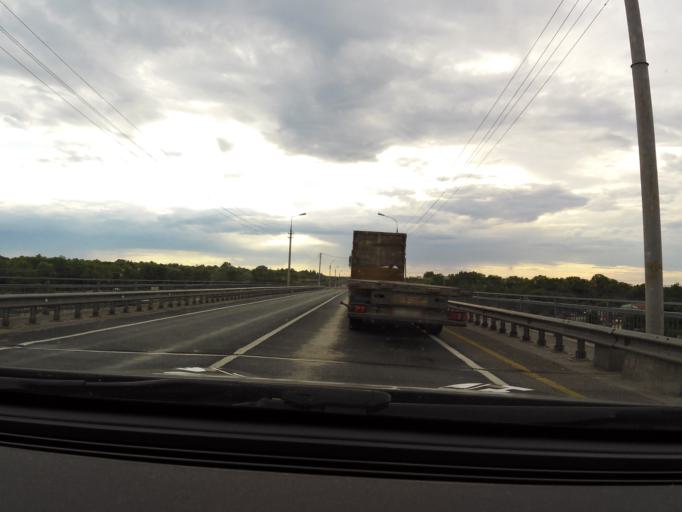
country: RU
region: Vladimir
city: Kommunar
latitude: 56.0556
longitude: 40.4027
